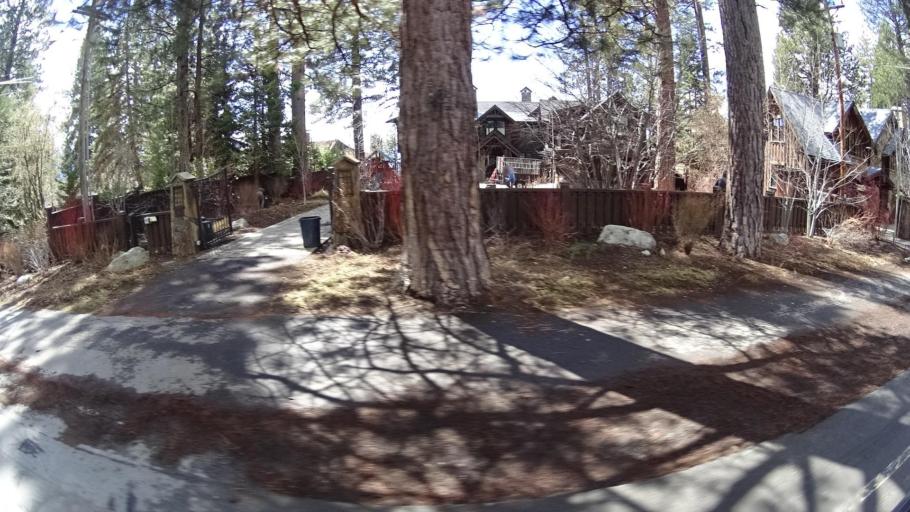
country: US
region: Nevada
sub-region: Washoe County
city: Incline Village
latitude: 39.2418
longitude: -119.9516
